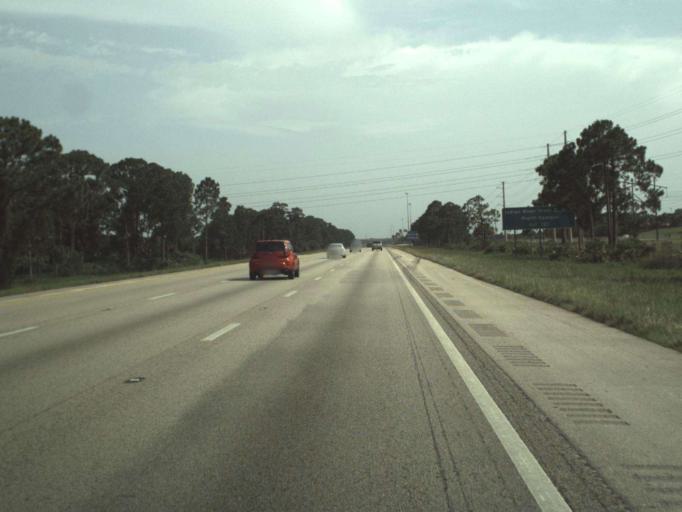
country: US
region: Florida
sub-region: Saint Lucie County
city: River Park
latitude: 27.3232
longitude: -80.4145
